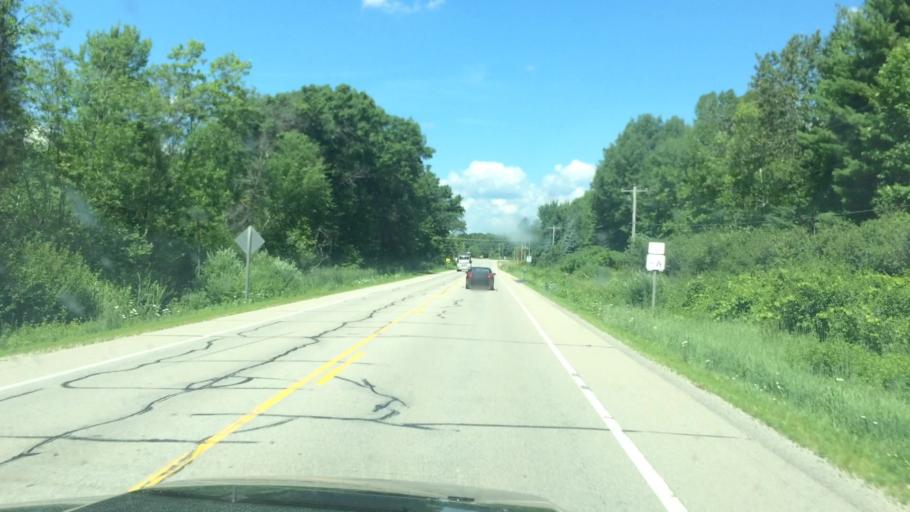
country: US
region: Wisconsin
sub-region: Marinette County
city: Peshtigo
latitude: 45.1025
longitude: -87.7467
